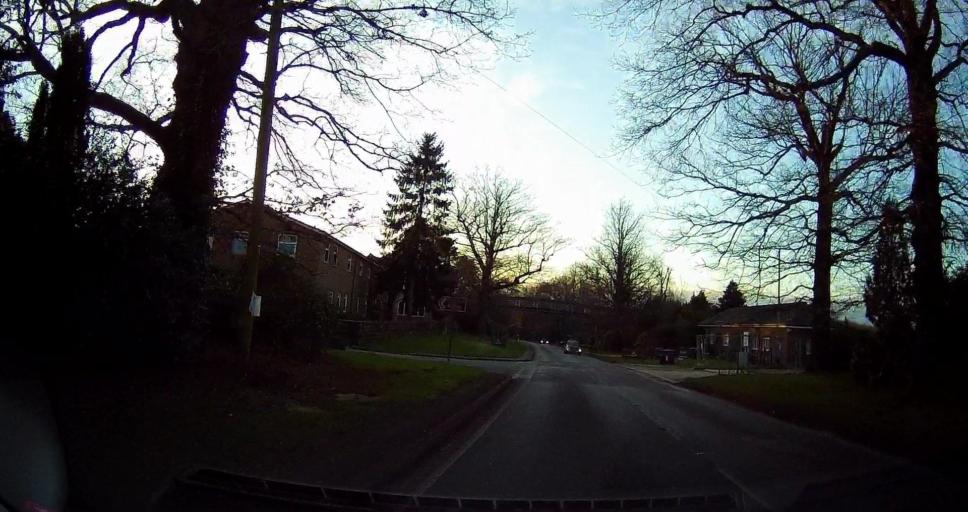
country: GB
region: England
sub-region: West Sussex
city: Maidenbower
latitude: 51.0944
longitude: -0.1179
